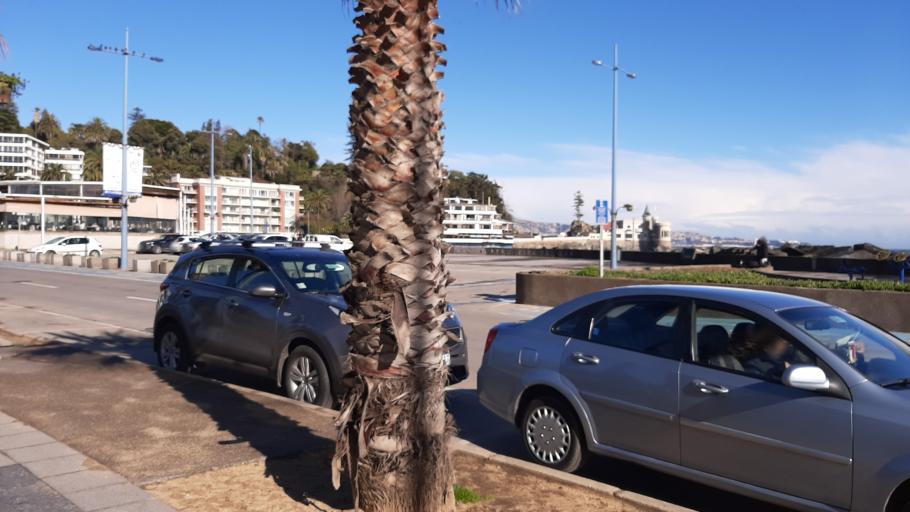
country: CL
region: Valparaiso
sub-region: Provincia de Valparaiso
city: Vina del Mar
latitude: -33.0185
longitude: -71.5613
